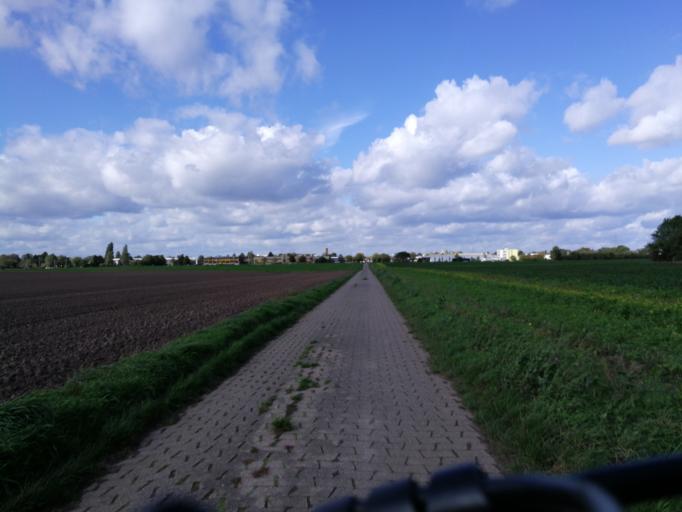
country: DE
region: North Rhine-Westphalia
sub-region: Regierungsbezirk Dusseldorf
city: Dusseldorf
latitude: 51.1513
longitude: 6.7501
